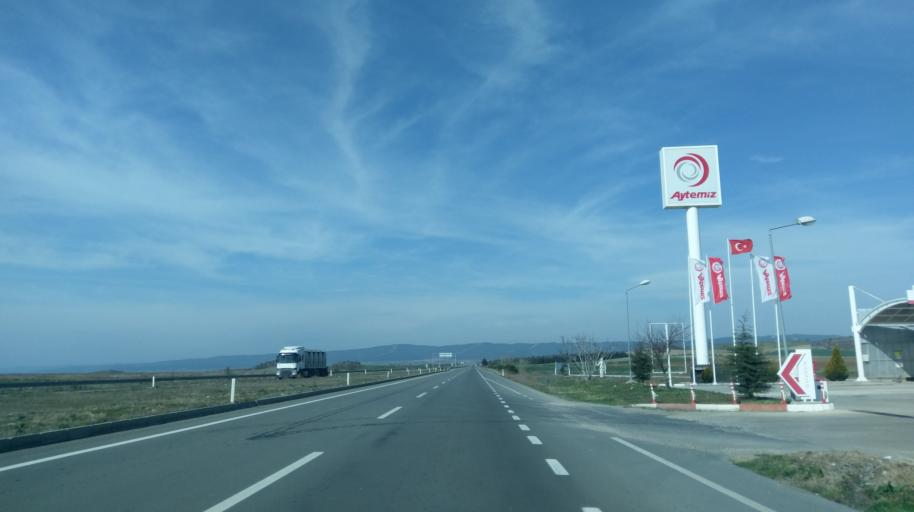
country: TR
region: Canakkale
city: Evrese
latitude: 40.6400
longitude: 26.8583
